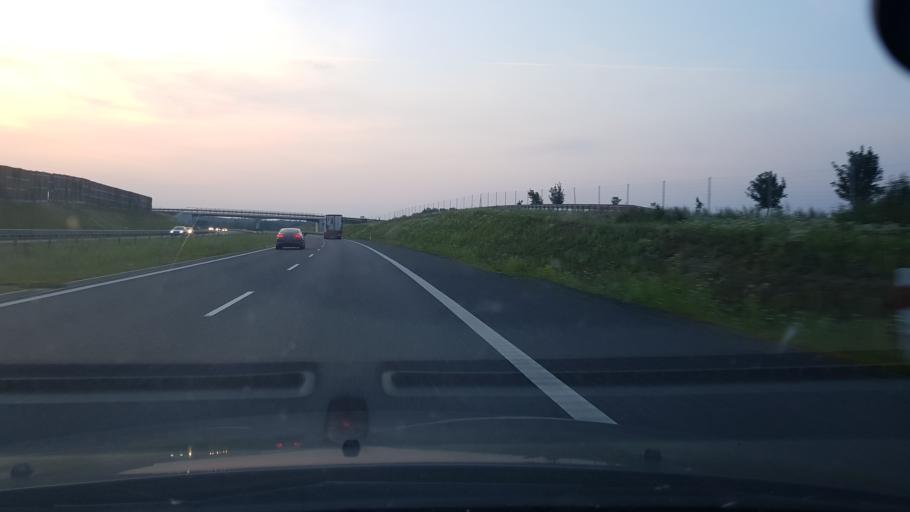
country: PL
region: Warmian-Masurian Voivodeship
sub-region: Powiat nidzicki
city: Nidzica
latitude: 53.4408
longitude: 20.3386
